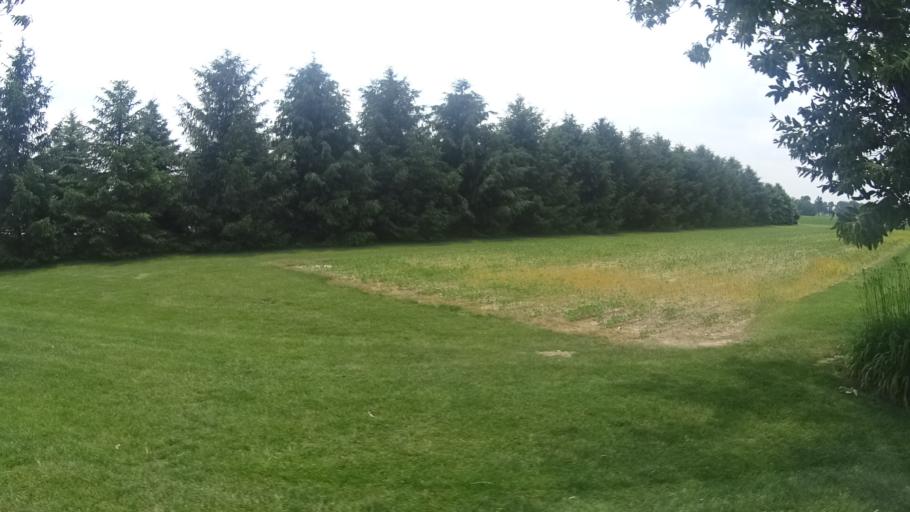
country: US
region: Ohio
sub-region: Erie County
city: Milan
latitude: 41.3124
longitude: -82.6667
